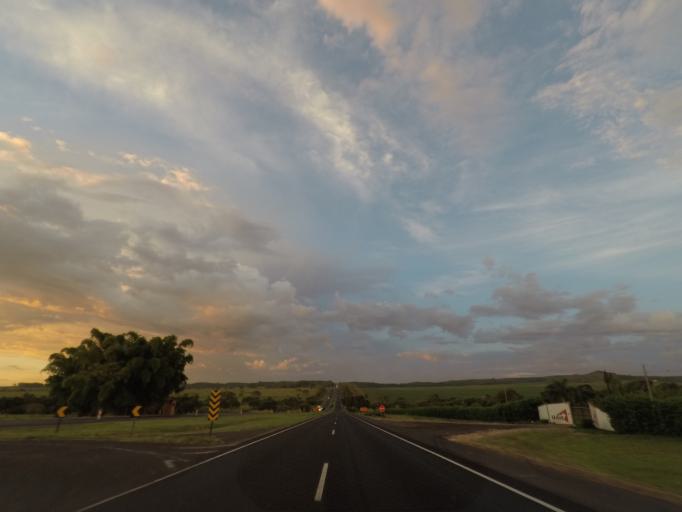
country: BR
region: Minas Gerais
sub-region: Uberaba
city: Uberaba
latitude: -19.6221
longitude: -48.0168
